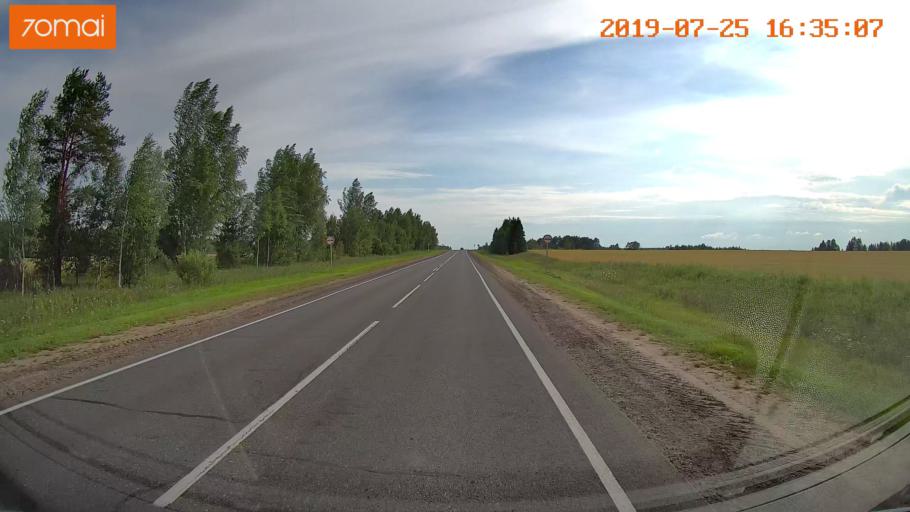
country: RU
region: Ivanovo
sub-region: Privolzhskiy Rayon
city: Ples
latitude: 57.4093
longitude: 41.4253
